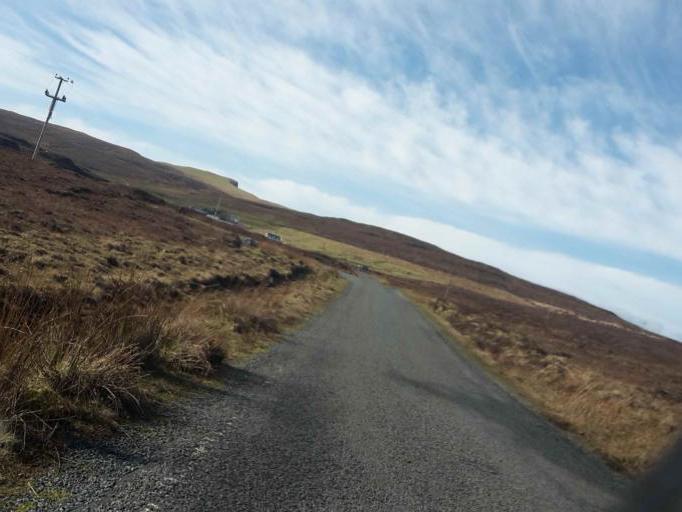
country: GB
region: Scotland
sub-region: Eilean Siar
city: Harris
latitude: 57.4449
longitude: -6.7249
